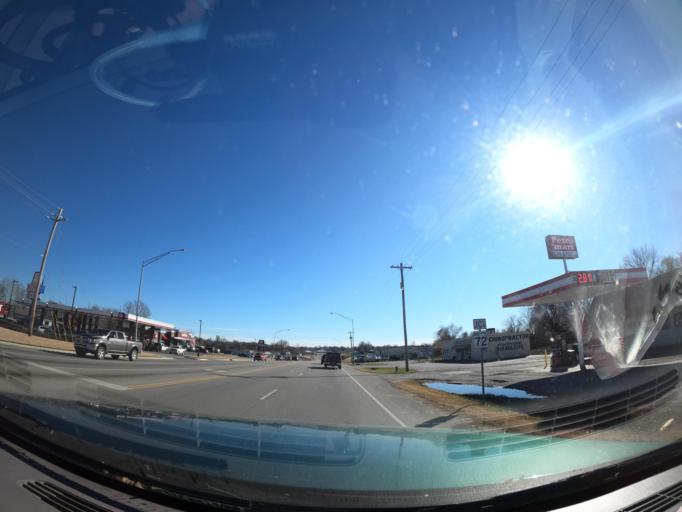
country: US
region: Oklahoma
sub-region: Wagoner County
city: Coweta
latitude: 35.9590
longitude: -95.6517
